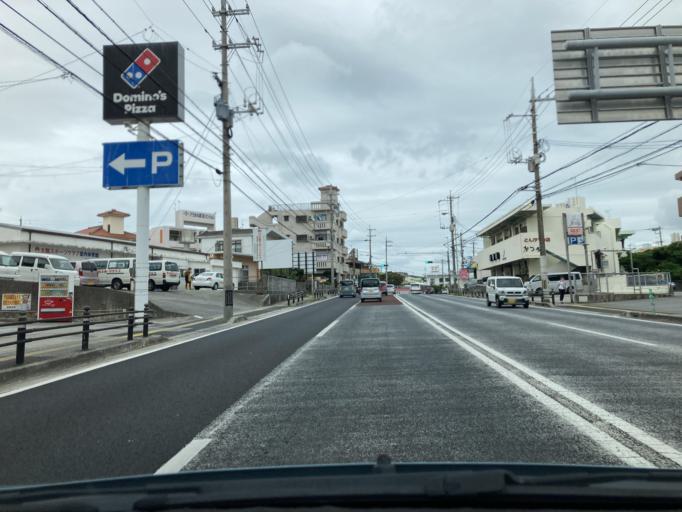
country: JP
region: Okinawa
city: Tomigusuku
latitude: 26.2008
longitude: 127.7423
